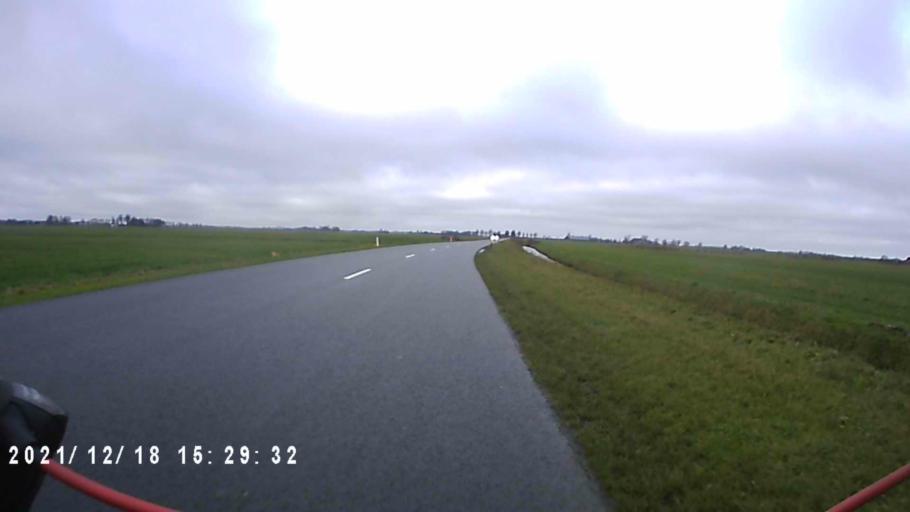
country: NL
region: Friesland
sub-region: Gemeente Dongeradeel
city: Anjum
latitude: 53.3346
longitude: 6.1411
